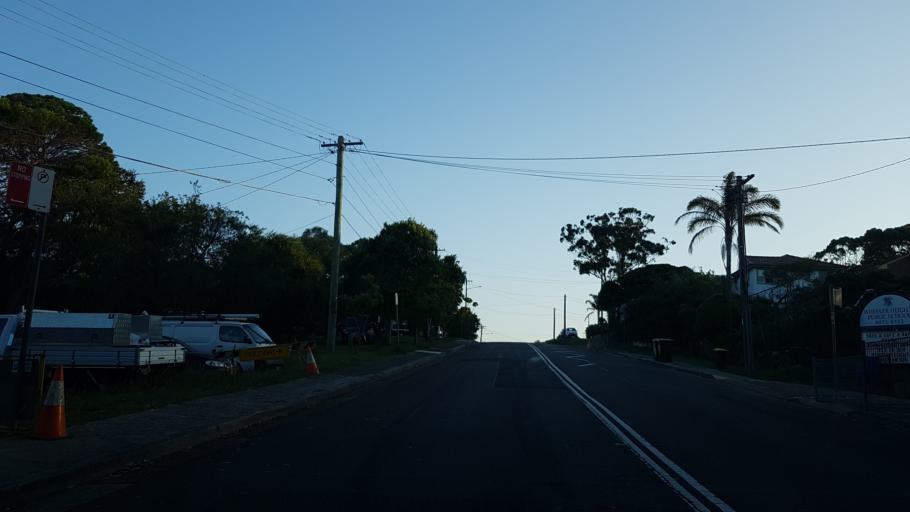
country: AU
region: New South Wales
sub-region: Warringah
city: Narrabeen
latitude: -33.7281
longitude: 151.2864
